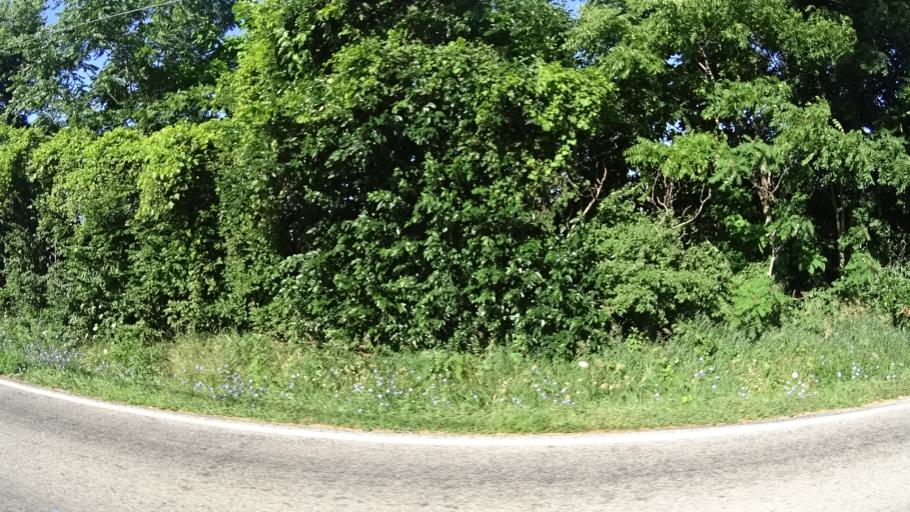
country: US
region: Ohio
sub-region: Erie County
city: Sandusky
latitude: 41.3748
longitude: -82.7679
